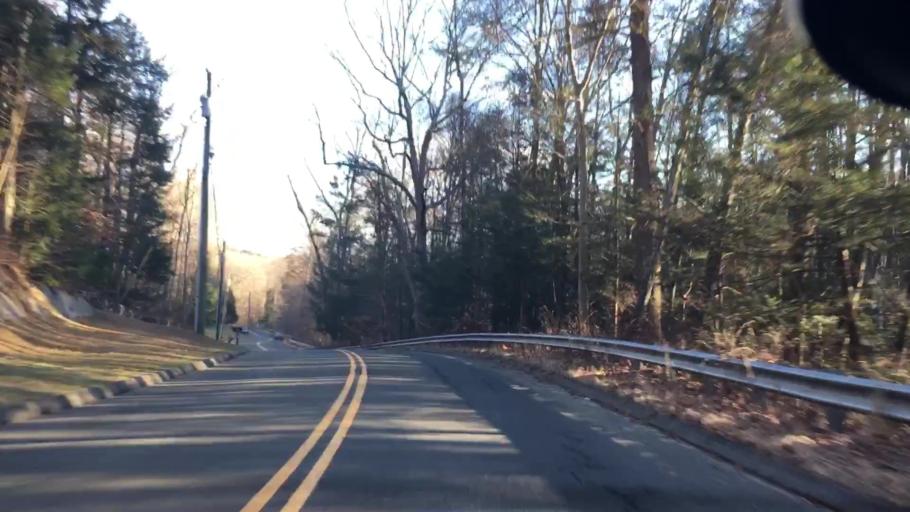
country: US
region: Connecticut
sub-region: Fairfield County
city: Newtown
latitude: 41.4628
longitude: -73.3318
